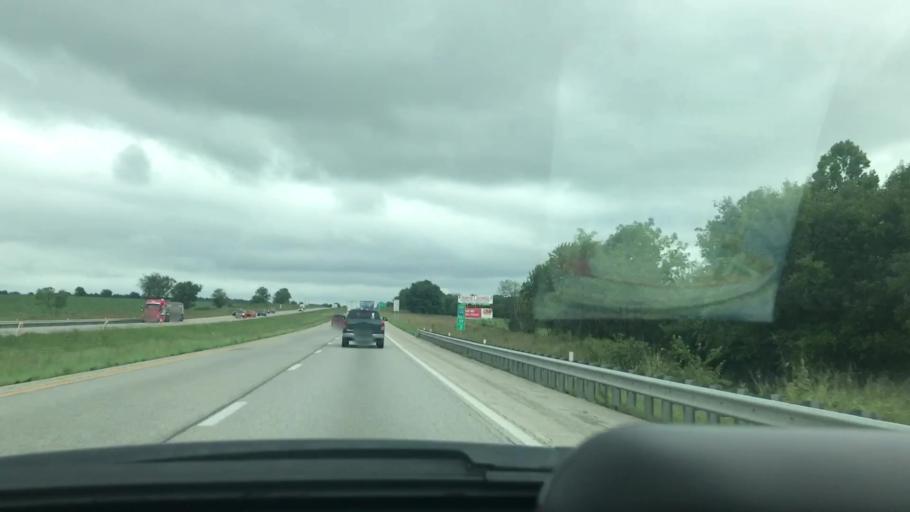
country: US
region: Missouri
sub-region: Greene County
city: Ash Grove
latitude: 37.1872
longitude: -93.6236
